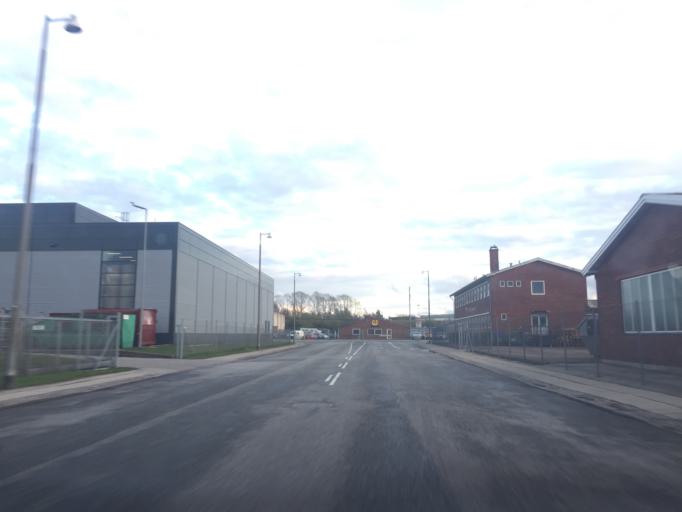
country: DK
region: Capital Region
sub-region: Albertslund Kommune
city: Albertslund
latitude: 55.6624
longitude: 12.3734
